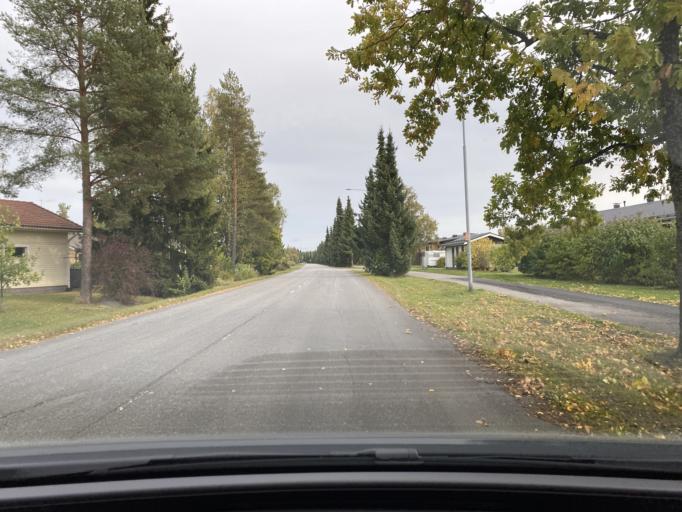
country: FI
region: Satakunta
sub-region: Pori
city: Huittinen
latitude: 61.1739
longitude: 22.6991
